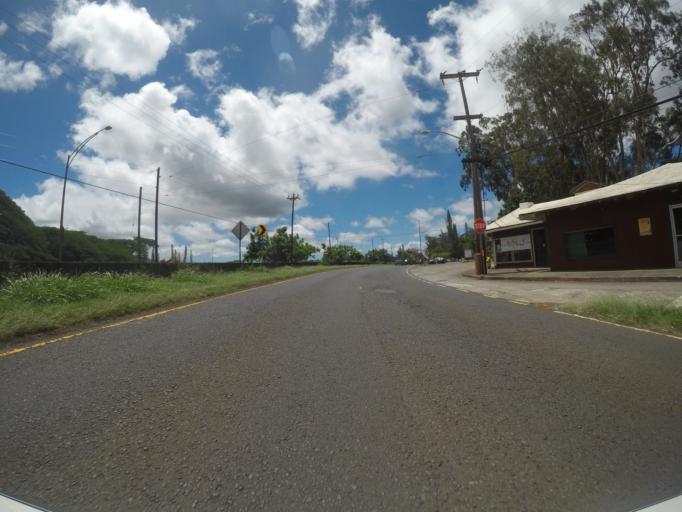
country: US
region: Hawaii
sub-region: Honolulu County
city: Schofield Barracks
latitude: 21.4948
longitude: -158.0504
